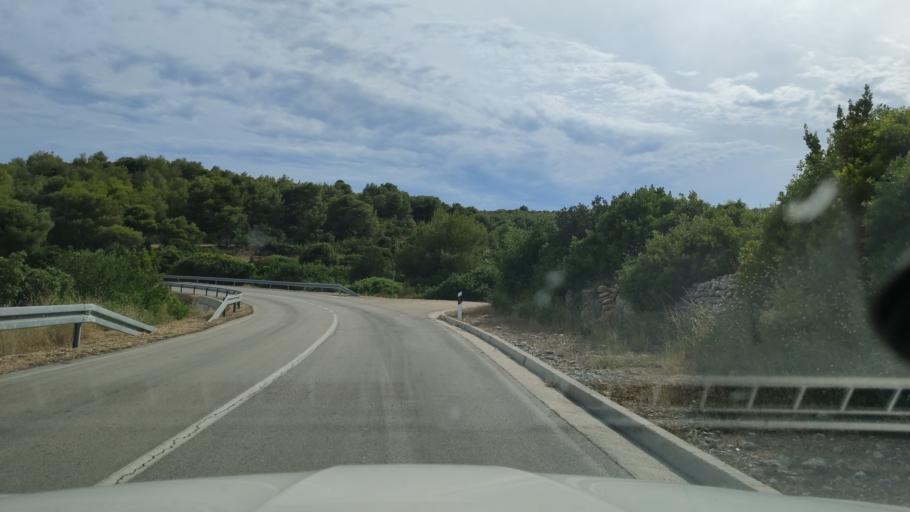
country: HR
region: Splitsko-Dalmatinska
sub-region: Grad Vis
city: Vis
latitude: 43.0340
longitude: 16.2018
